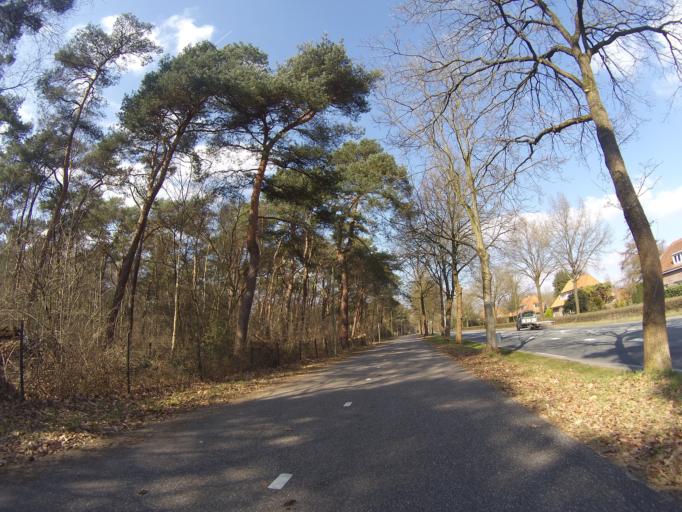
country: NL
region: Utrecht
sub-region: Gemeente Zeist
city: Zeist
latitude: 52.1480
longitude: 5.2365
